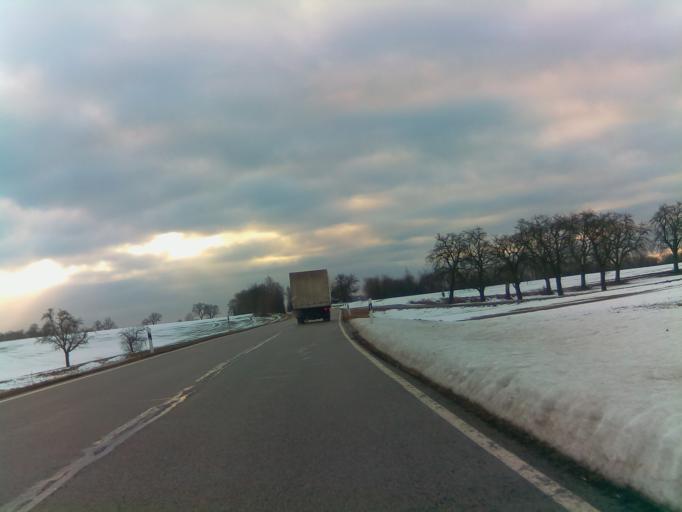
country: DE
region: Baden-Wuerttemberg
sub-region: Karlsruhe Region
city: Fahrenbach
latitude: 49.4624
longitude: 9.0936
